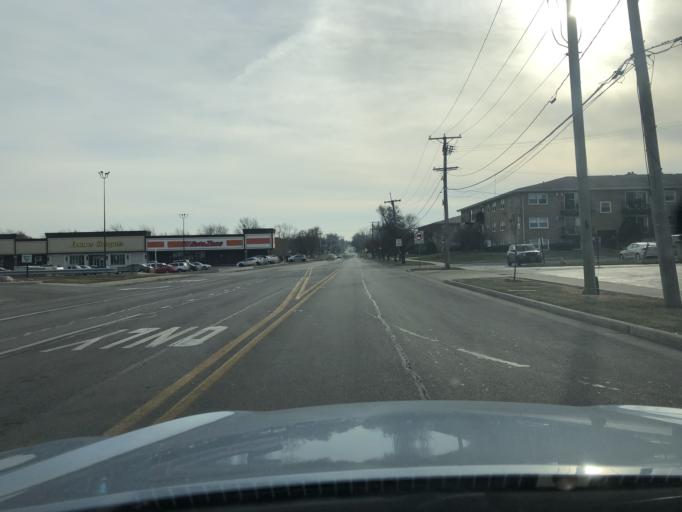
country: US
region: Illinois
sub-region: DuPage County
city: Addison
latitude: 41.9380
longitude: -88.0035
